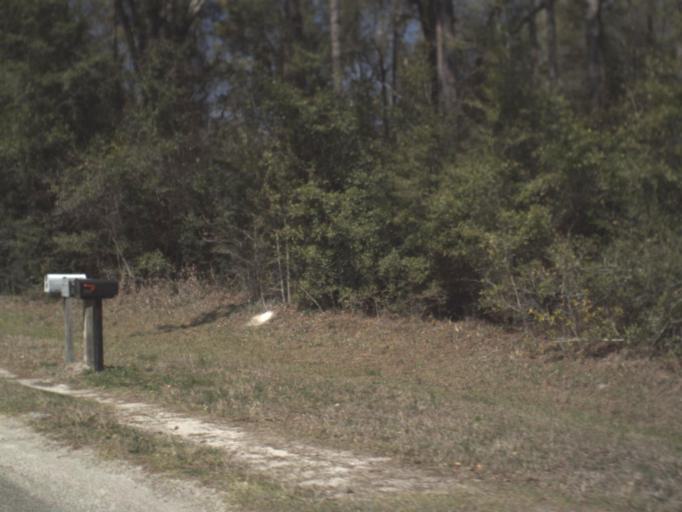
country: US
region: Florida
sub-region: Leon County
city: Woodville
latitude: 30.2282
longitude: -84.2192
